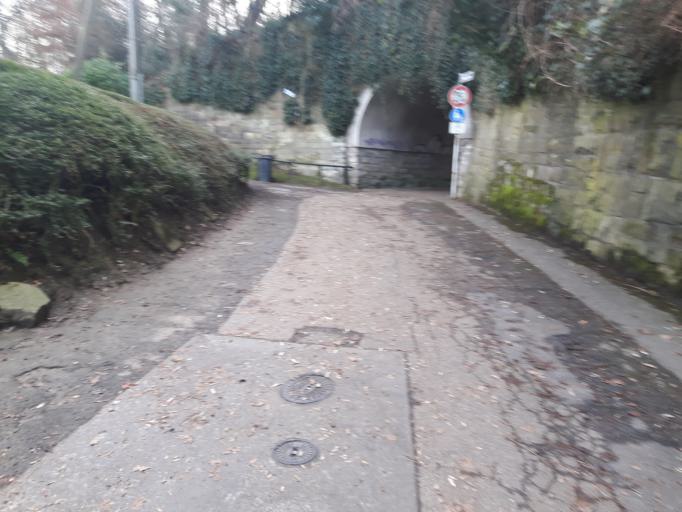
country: DE
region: North Rhine-Westphalia
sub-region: Regierungsbezirk Dusseldorf
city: Essen
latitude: 51.4281
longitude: 7.0290
